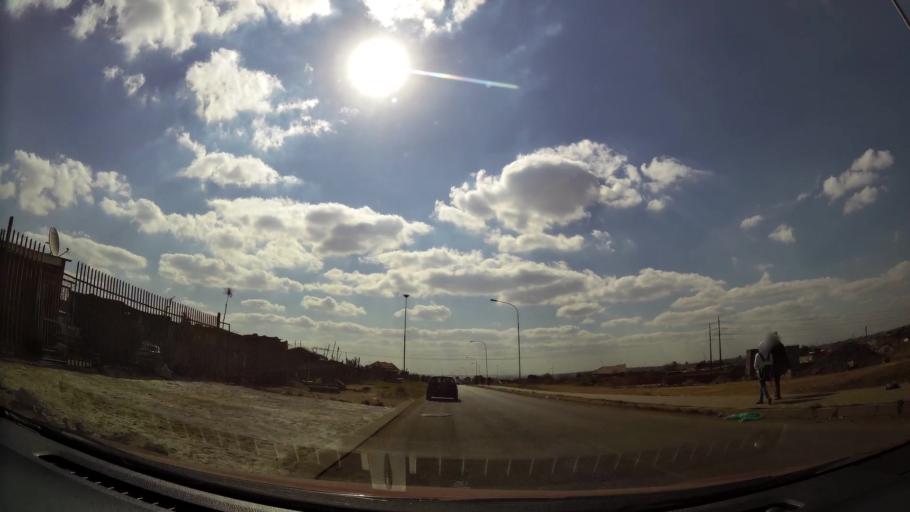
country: ZA
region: Gauteng
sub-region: Ekurhuleni Metropolitan Municipality
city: Tembisa
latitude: -25.9902
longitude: 28.2140
